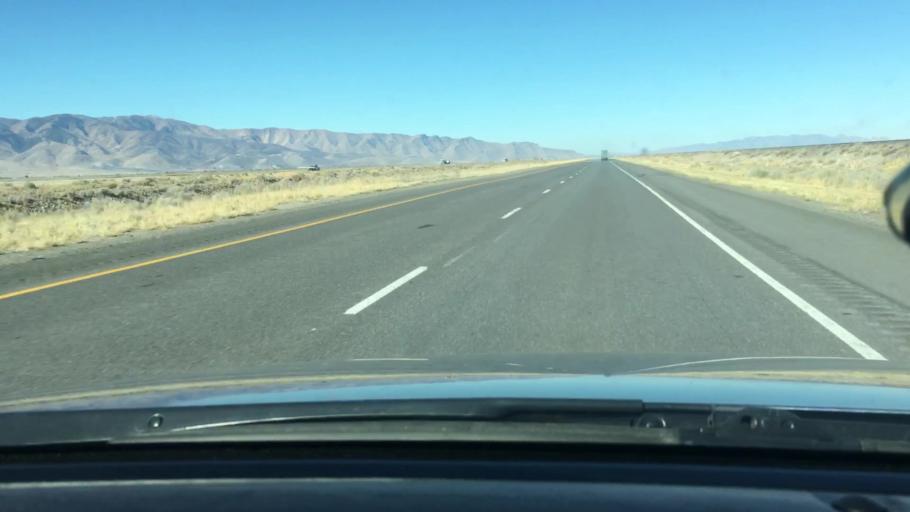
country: US
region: Utah
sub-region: Tooele County
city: Grantsville
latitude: 40.6747
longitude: -112.3976
